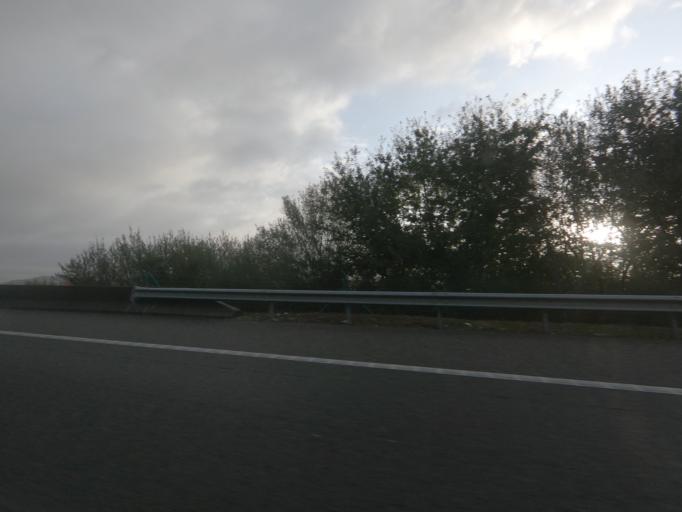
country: ES
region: Galicia
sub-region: Provincia de Pontevedra
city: Porrino
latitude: 42.1746
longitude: -8.6502
